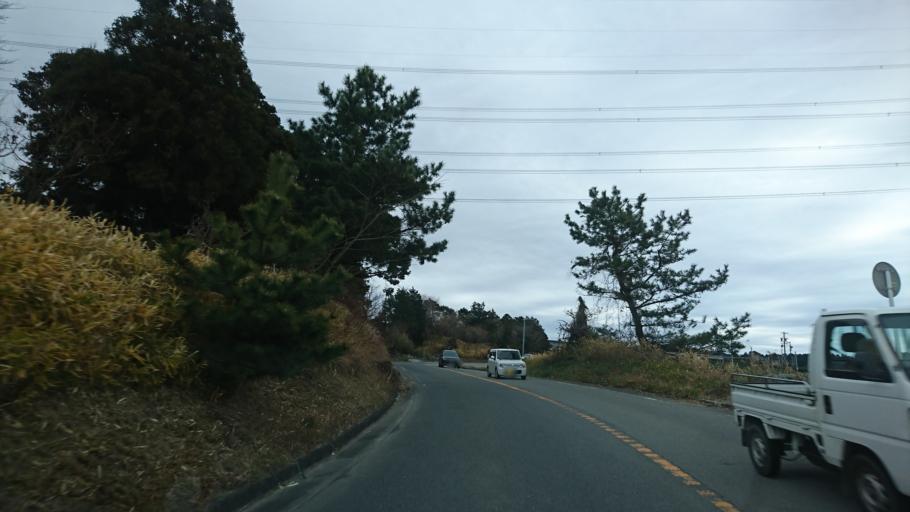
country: JP
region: Shizuoka
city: Kanaya
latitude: 34.7811
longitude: 138.1312
